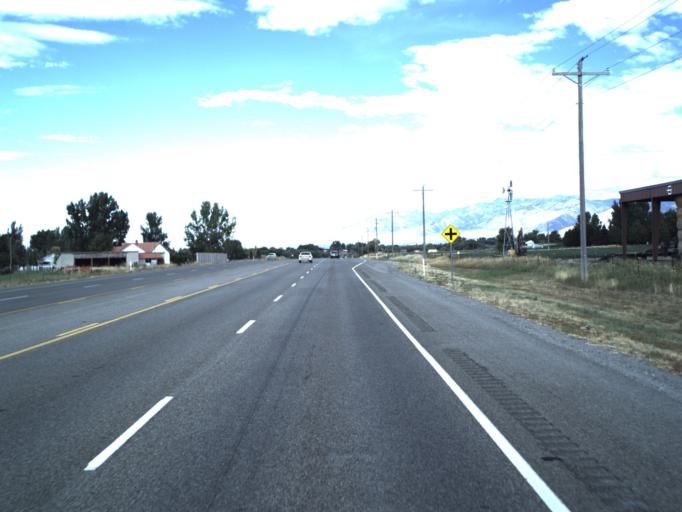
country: US
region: Utah
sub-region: Cache County
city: Wellsville
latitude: 41.6320
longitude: -111.9223
